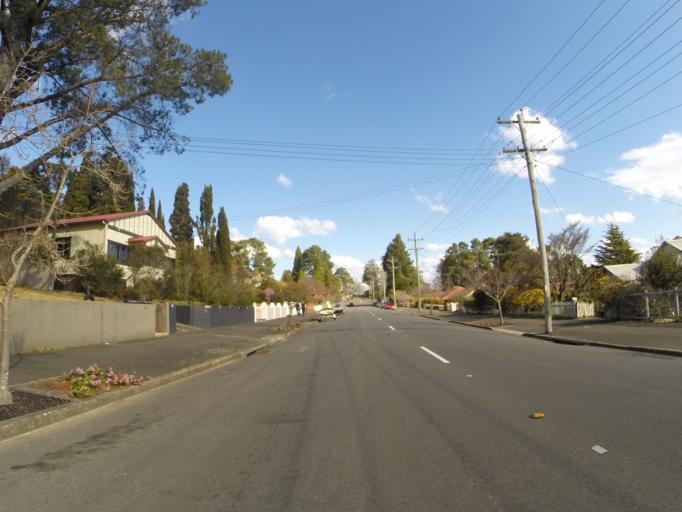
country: AU
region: New South Wales
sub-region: Blue Mountains Municipality
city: Katoomba
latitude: -33.7256
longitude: 150.3093
